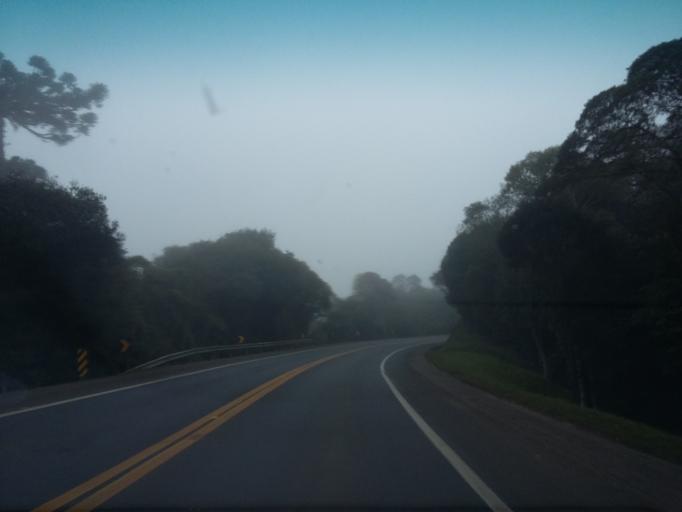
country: BR
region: Santa Catarina
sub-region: Curitibanos
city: Curitibanos
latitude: -27.2941
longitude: -50.4323
